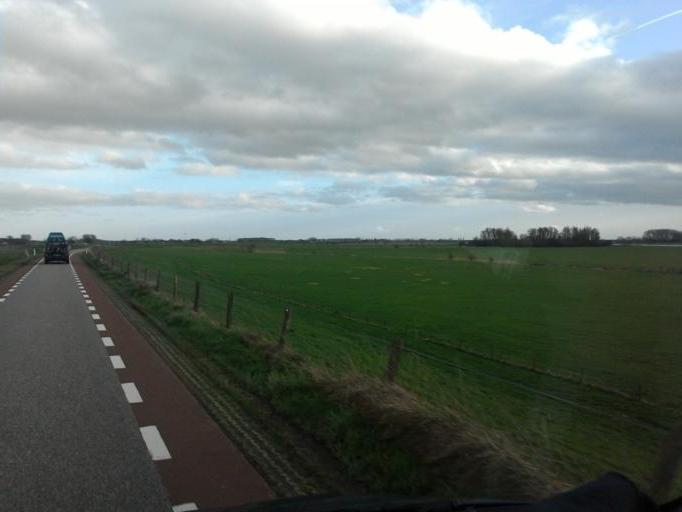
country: NL
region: Gelderland
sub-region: Gemeente Culemborg
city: Culemborg
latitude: 51.9817
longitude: 5.2482
